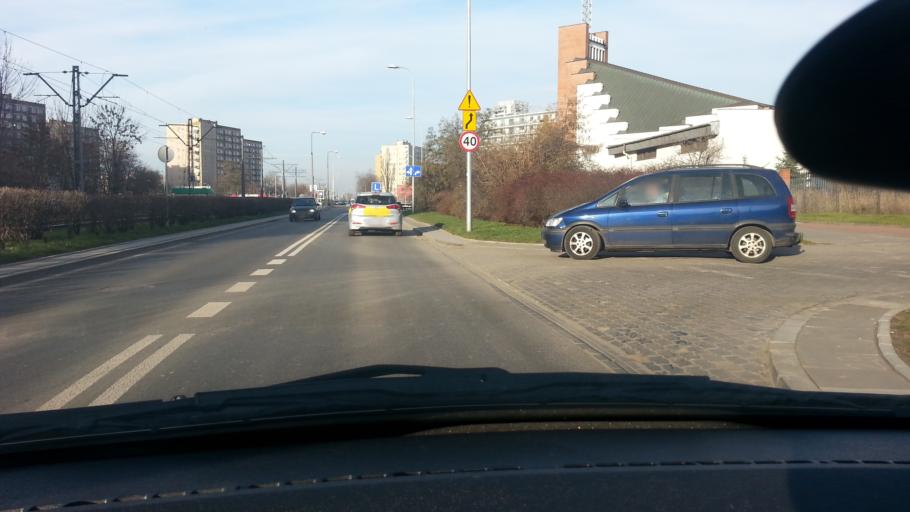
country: PL
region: Masovian Voivodeship
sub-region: Warszawa
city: Targowek
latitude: 52.2919
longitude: 21.0284
